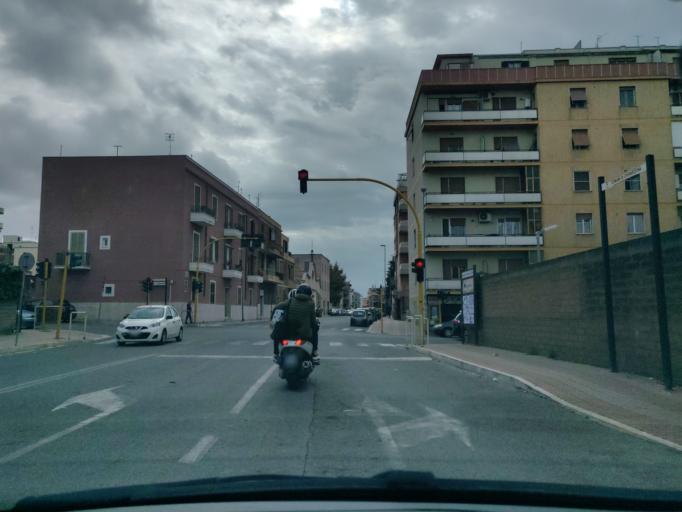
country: IT
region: Latium
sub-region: Citta metropolitana di Roma Capitale
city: Civitavecchia
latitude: 42.0964
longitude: 11.8026
